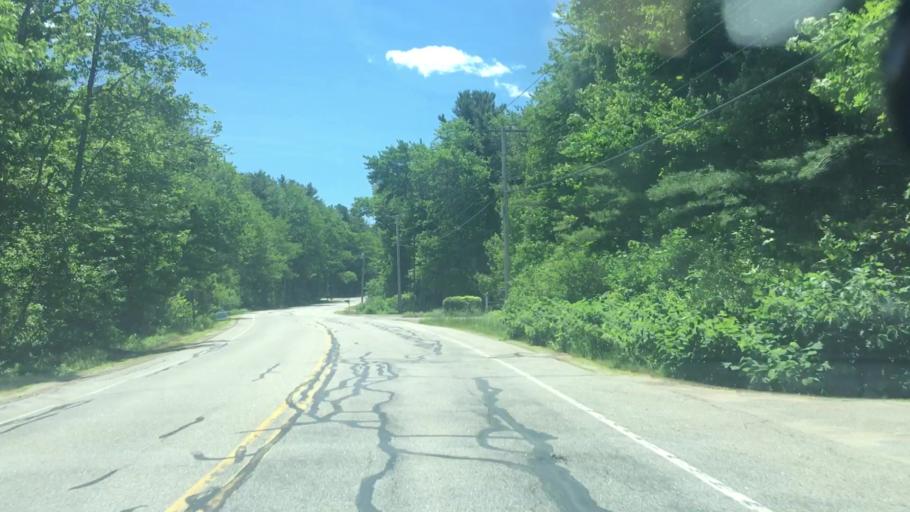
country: US
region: Maine
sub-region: York County
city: Kennebunk
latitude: 43.3780
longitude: -70.5280
